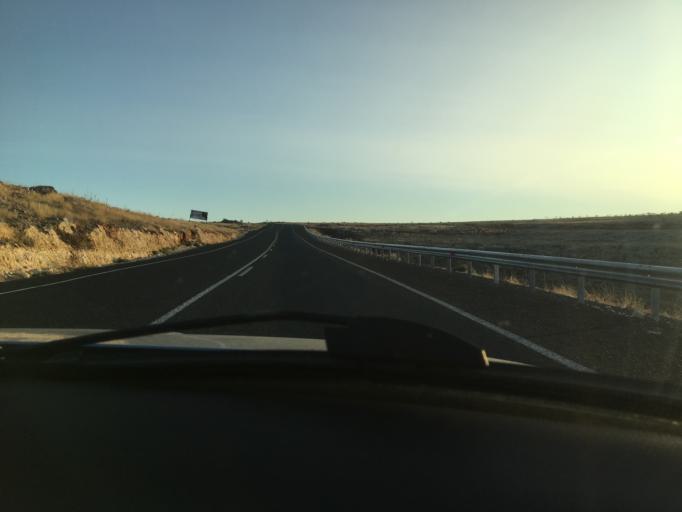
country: TR
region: Sanliurfa
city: Bogurtlen
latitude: 37.1825
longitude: 37.9756
